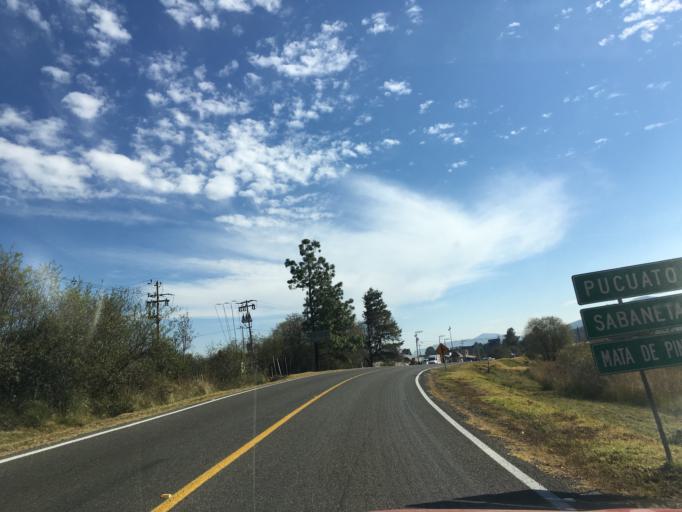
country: MX
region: Michoacan
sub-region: Hidalgo
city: Tierras Coloradas (San Pedro)
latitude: 19.6688
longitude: -100.7094
